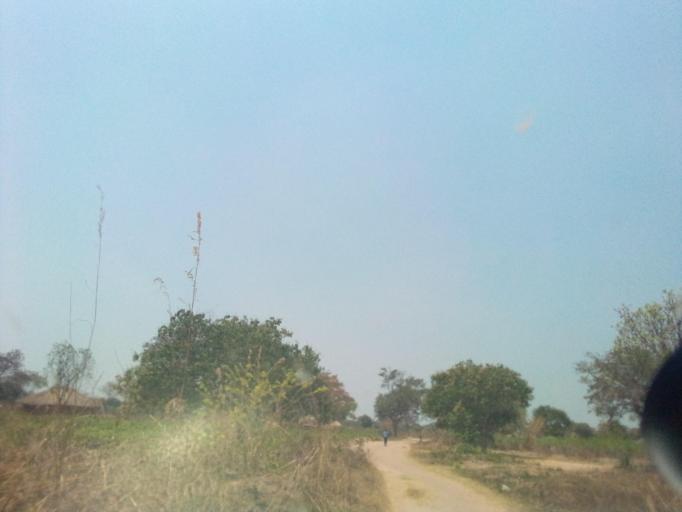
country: ZM
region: Copperbelt
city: Kataba
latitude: -12.2411
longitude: 30.3170
